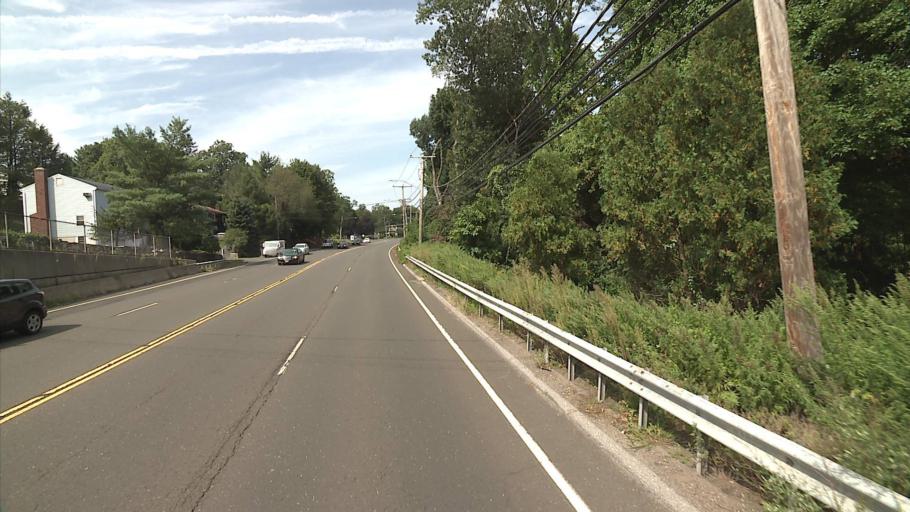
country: US
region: Connecticut
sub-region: Fairfield County
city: Stamford
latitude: 41.0868
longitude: -73.5579
